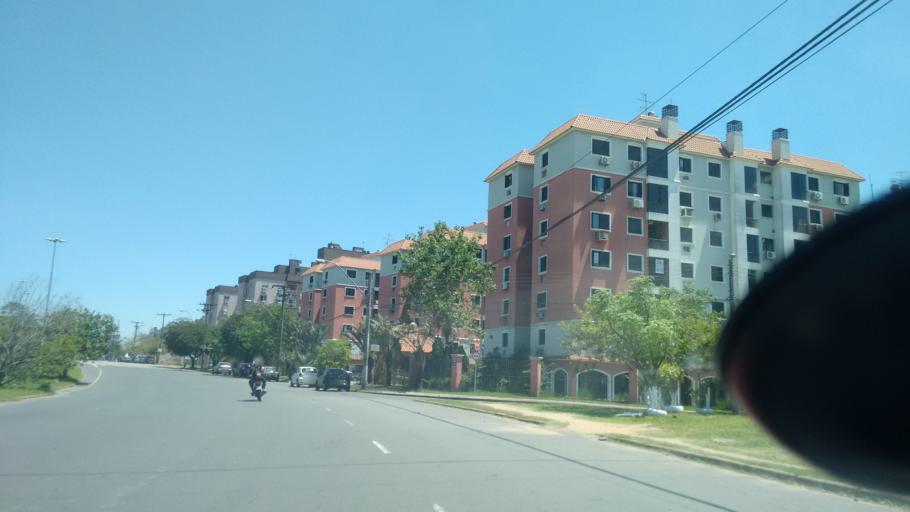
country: BR
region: Rio Grande do Sul
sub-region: Cachoeirinha
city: Cachoeirinha
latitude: -30.0018
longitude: -51.1280
